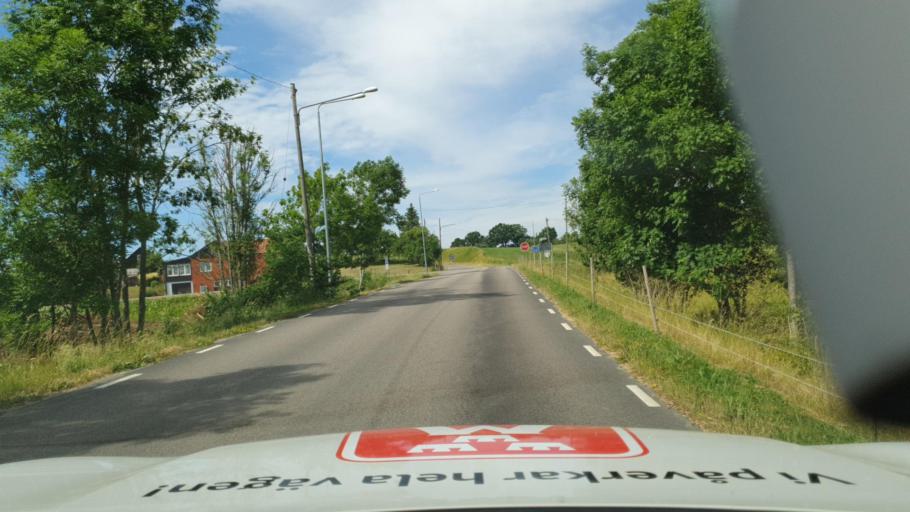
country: SE
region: Skane
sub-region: Sjobo Kommun
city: Sjoebo
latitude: 55.6386
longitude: 13.7752
